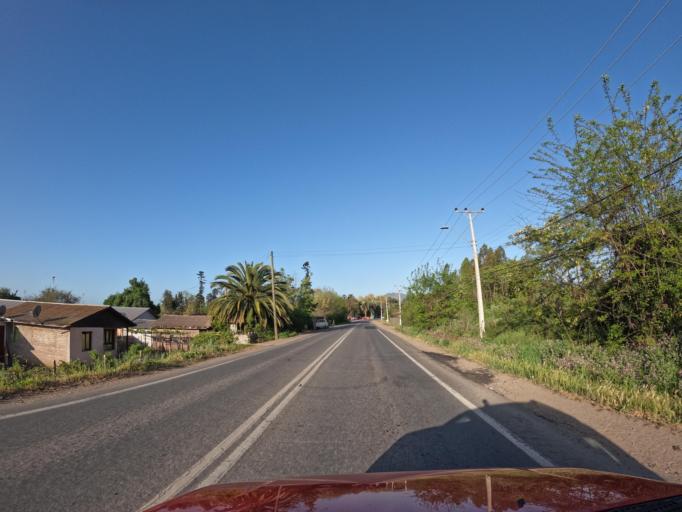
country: CL
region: O'Higgins
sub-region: Provincia de Colchagua
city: Santa Cruz
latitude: -34.5214
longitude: -71.3792
